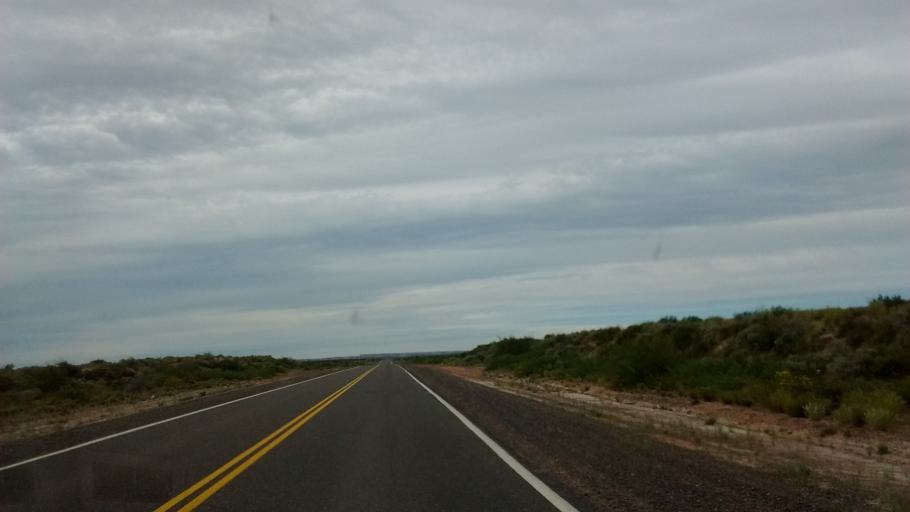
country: AR
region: Rio Negro
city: Catriel
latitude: -38.0849
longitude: -67.9254
